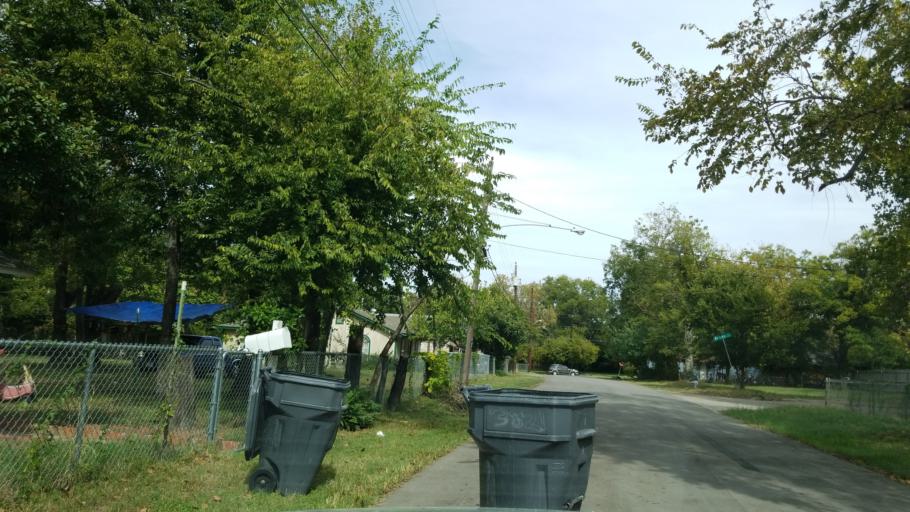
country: US
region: Texas
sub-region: Dallas County
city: Dallas
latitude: 32.7644
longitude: -96.7377
